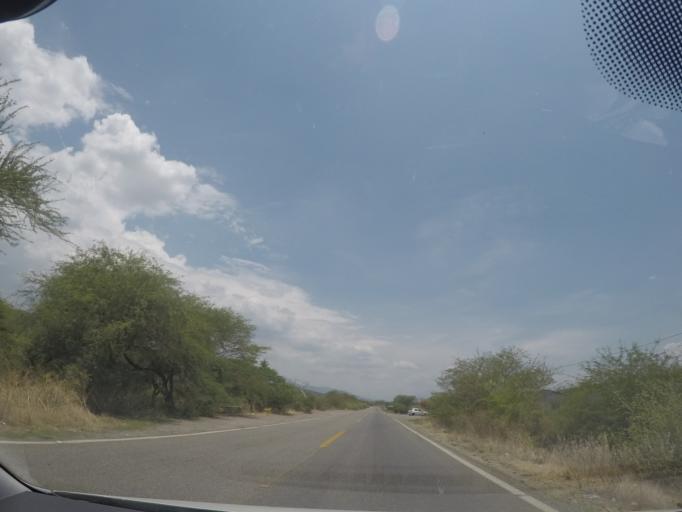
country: MX
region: Oaxaca
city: Magdalena Tequisistlan
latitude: 16.4321
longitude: -95.5328
